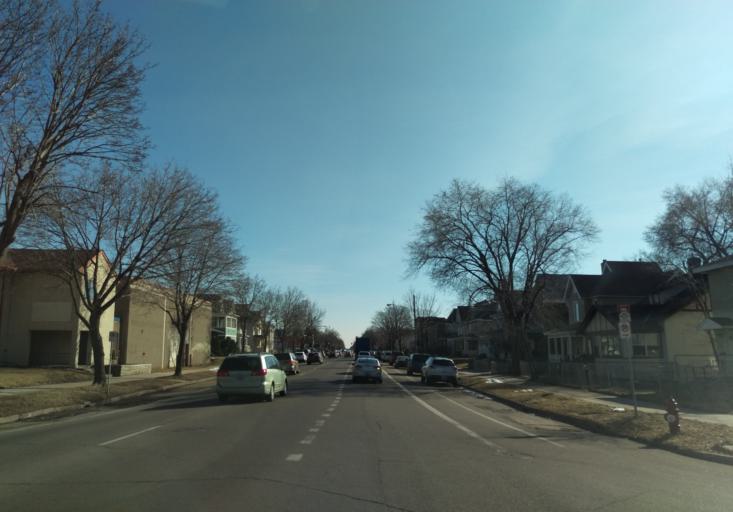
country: US
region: Minnesota
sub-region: Hennepin County
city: Minneapolis
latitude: 44.9501
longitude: -93.2678
